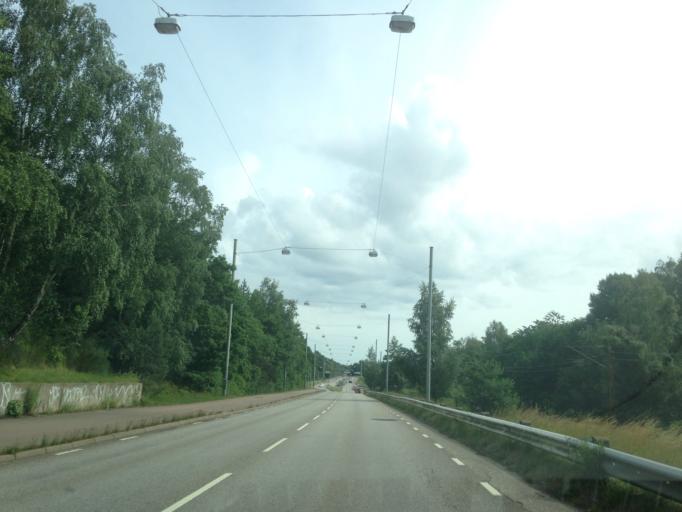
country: SE
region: Vaestra Goetaland
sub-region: Goteborg
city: Goeteborg
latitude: 57.7527
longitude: 11.9481
